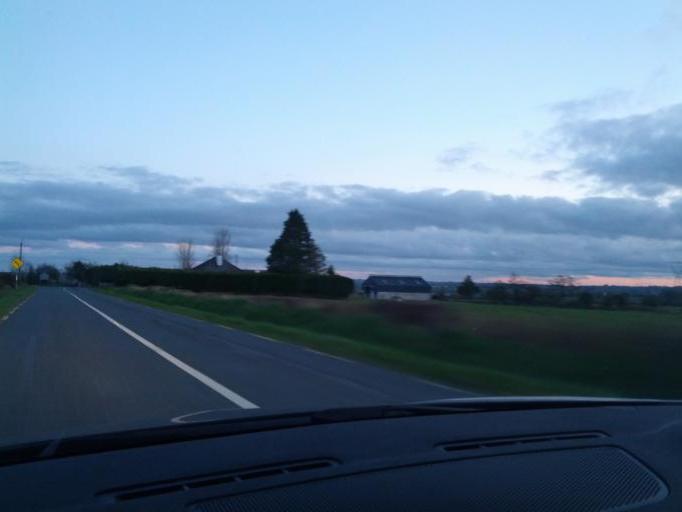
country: IE
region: Connaught
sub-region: Roscommon
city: Boyle
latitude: 53.8438
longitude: -8.2243
